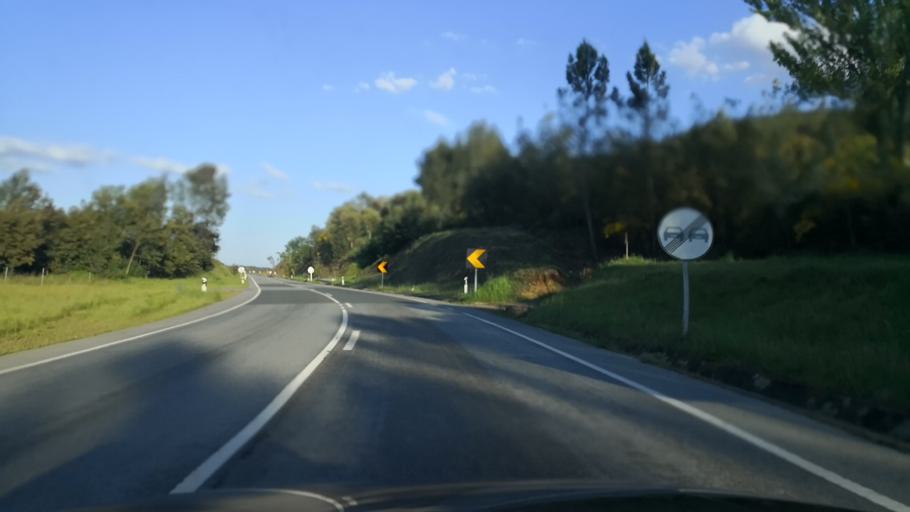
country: PT
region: Portalegre
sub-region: Marvao
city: Marvao
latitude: 39.3804
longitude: -7.3756
